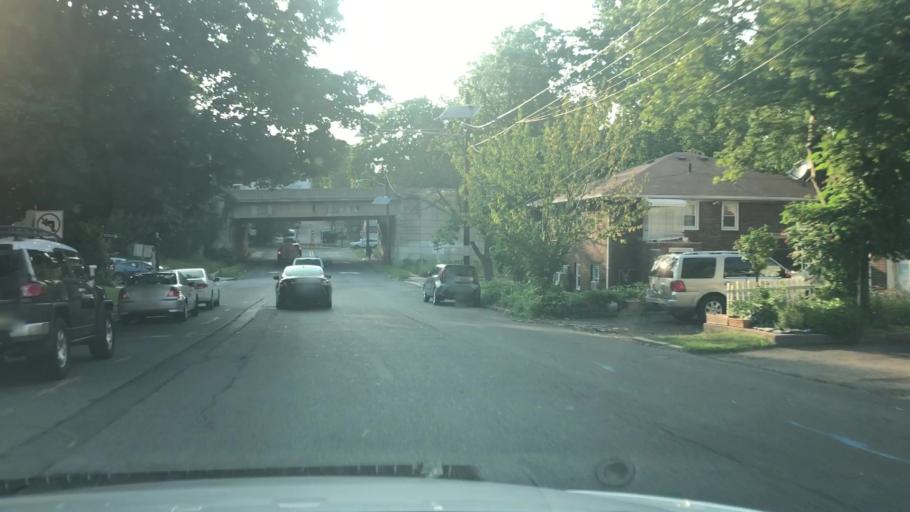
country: US
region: New Jersey
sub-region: Bergen County
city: Palisades Park
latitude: 40.8420
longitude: -73.9937
